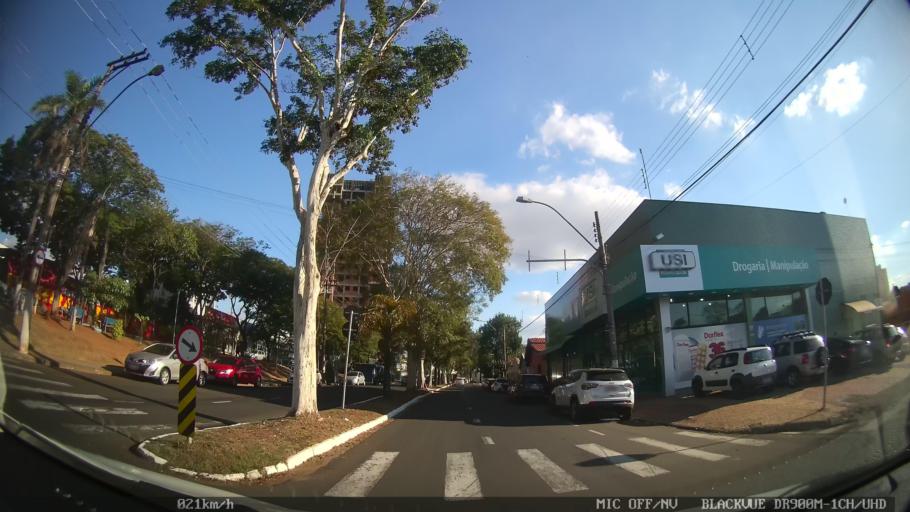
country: BR
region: Sao Paulo
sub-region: Santa Barbara D'Oeste
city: Santa Barbara d'Oeste
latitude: -22.7494
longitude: -47.4151
